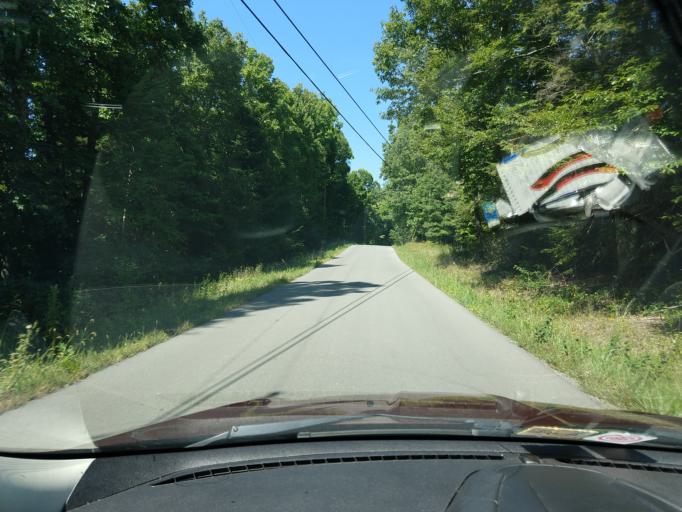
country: US
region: West Virginia
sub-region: Nicholas County
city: Craigsville
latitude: 38.2744
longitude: -80.7142
